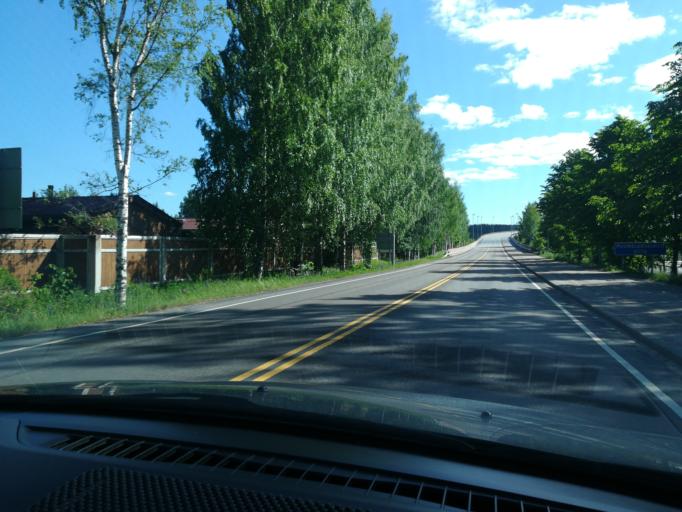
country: FI
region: Southern Savonia
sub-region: Mikkeli
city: Puumala
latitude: 61.5235
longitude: 28.1813
